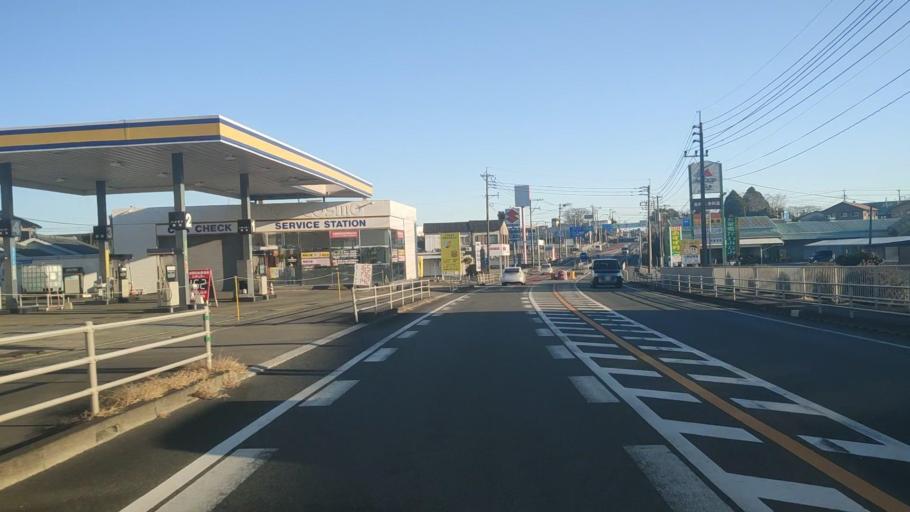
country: JP
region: Miyazaki
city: Takanabe
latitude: 32.1962
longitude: 131.5252
